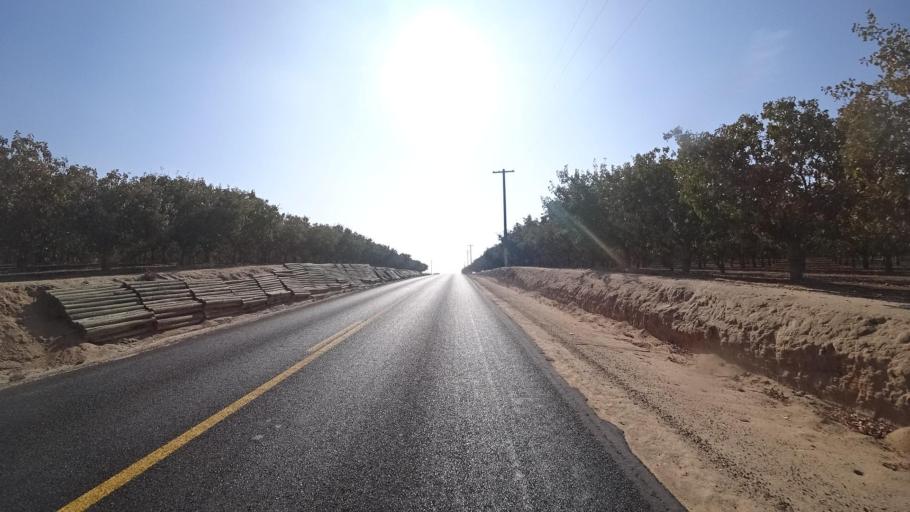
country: US
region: California
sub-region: Kern County
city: Shafter
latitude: 35.5496
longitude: -119.1512
